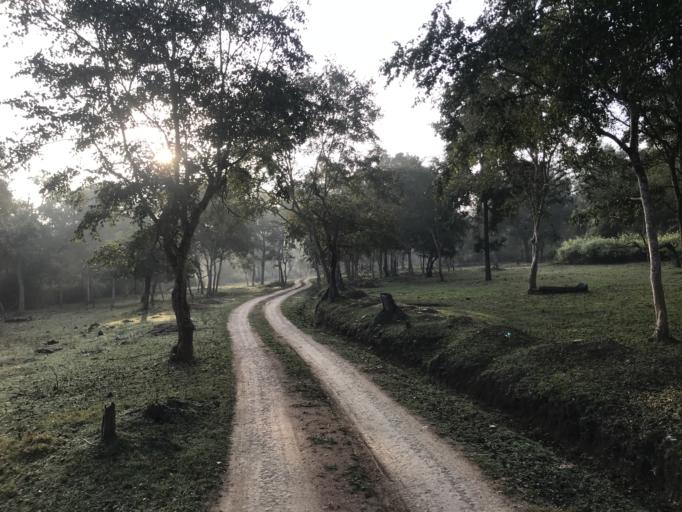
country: IN
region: Karnataka
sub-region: Mysore
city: Heggadadevankote
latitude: 12.0112
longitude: 76.2434
